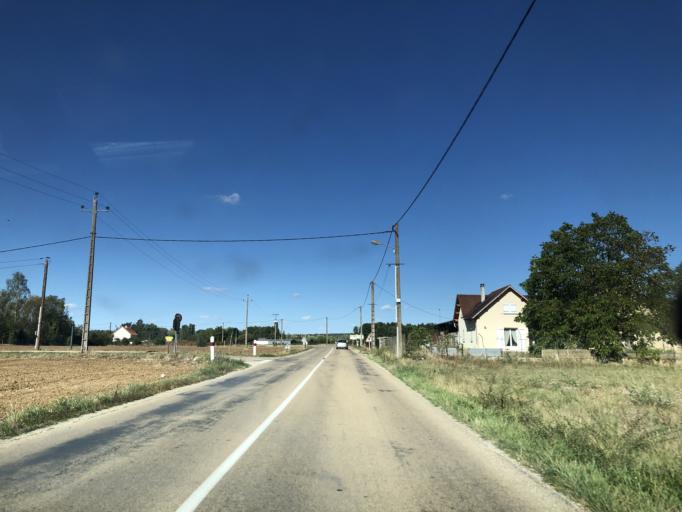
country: FR
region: Bourgogne
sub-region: Departement de l'Yonne
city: Appoigny
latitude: 47.8791
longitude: 3.5393
